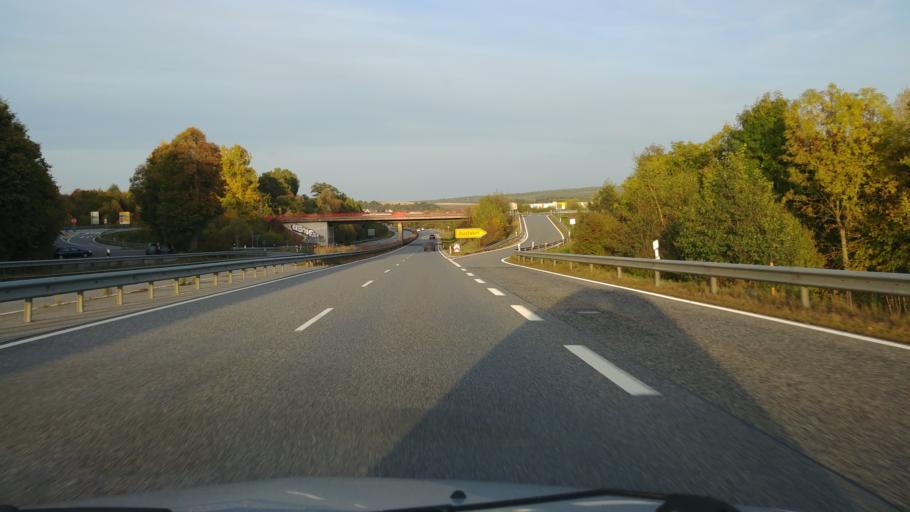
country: DE
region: Rheinland-Pfalz
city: Rheinbollen
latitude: 49.9943
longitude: 7.6557
